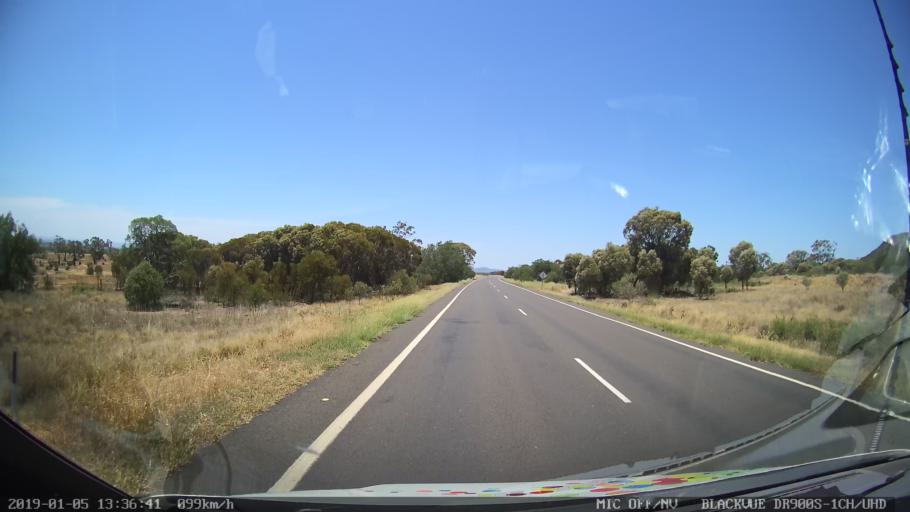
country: AU
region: New South Wales
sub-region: Gunnedah
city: Gunnedah
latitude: -30.9835
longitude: 150.1686
